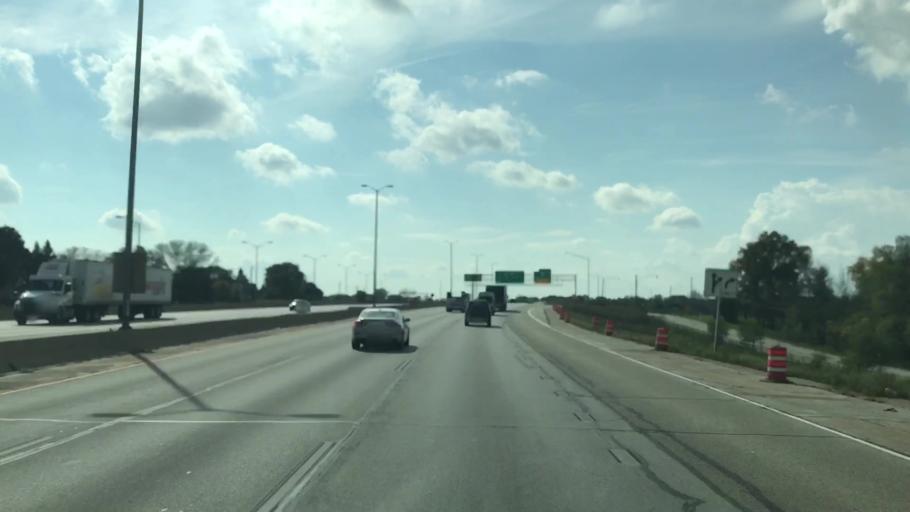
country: US
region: Wisconsin
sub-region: Waukesha County
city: Butler
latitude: 43.1408
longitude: -88.0551
